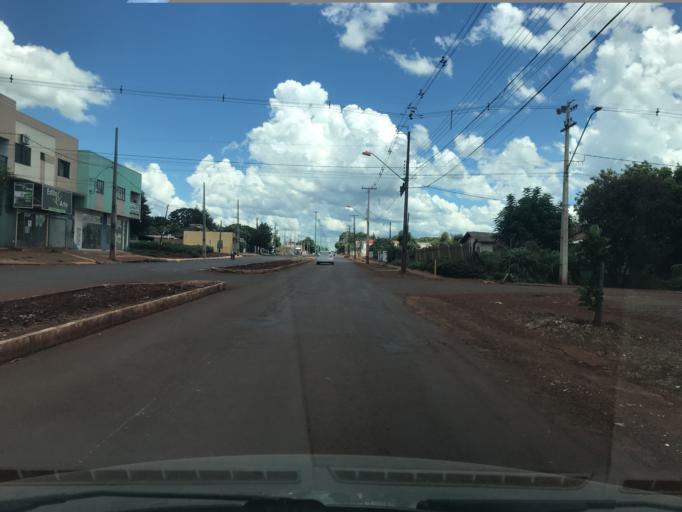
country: BR
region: Parana
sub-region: Palotina
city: Palotina
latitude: -24.2686
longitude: -53.8417
